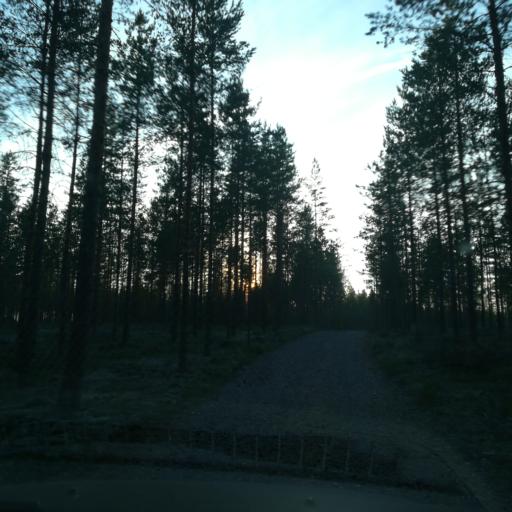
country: FI
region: Southern Savonia
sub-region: Mikkeli
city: Puumala
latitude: 61.4337
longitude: 28.4633
